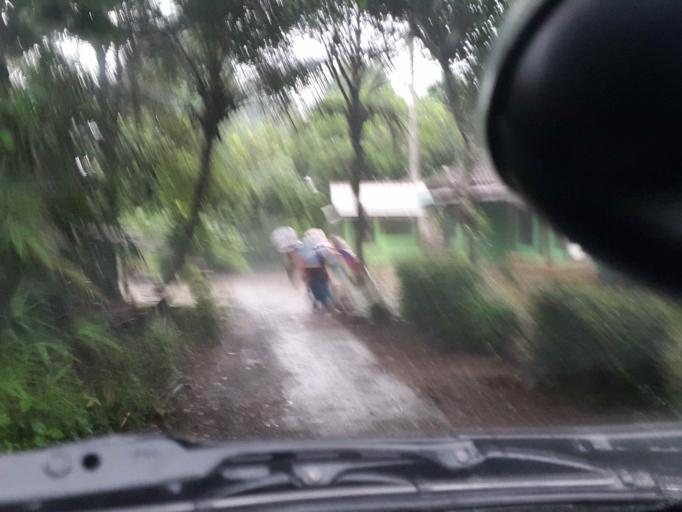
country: ID
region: Central Java
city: Kutoarjo
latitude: -7.5380
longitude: 109.9807
